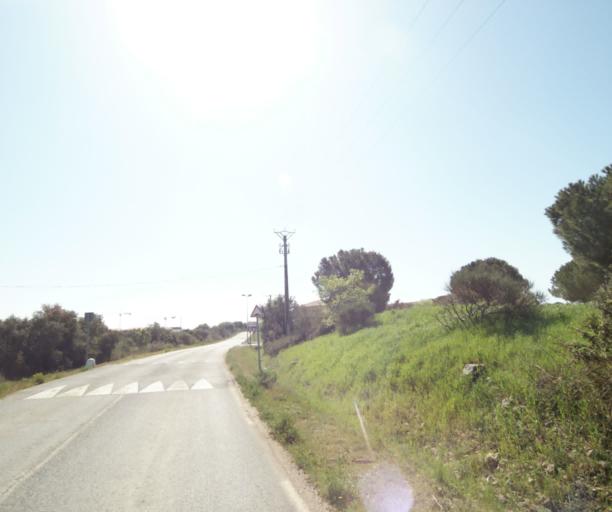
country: FR
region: Languedoc-Roussillon
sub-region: Departement de l'Herault
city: Saint-Bres
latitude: 43.6723
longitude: 4.0334
